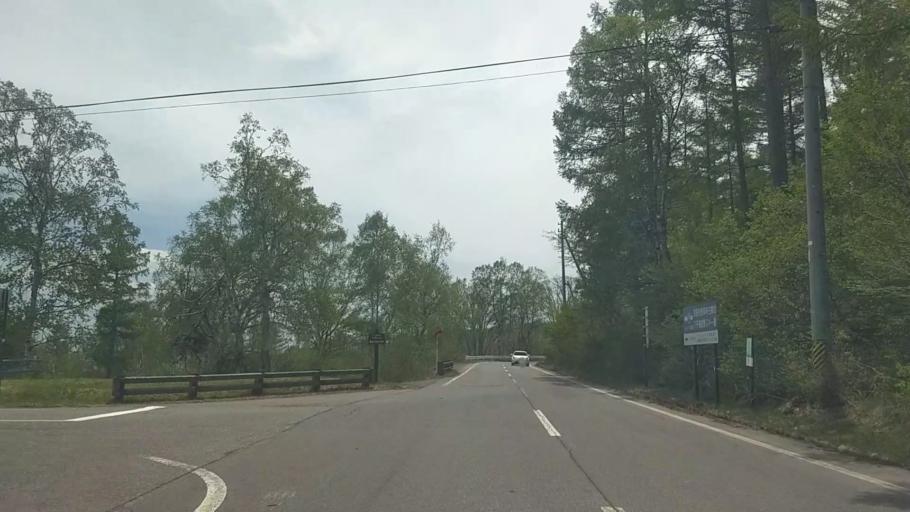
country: JP
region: Nagano
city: Saku
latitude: 36.0815
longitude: 138.3844
